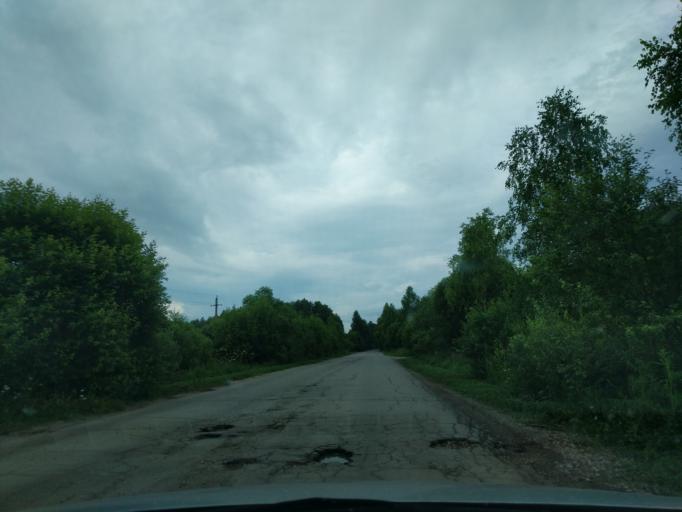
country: RU
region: Kaluga
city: Nikola-Lenivets
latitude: 54.7599
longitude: 35.7030
